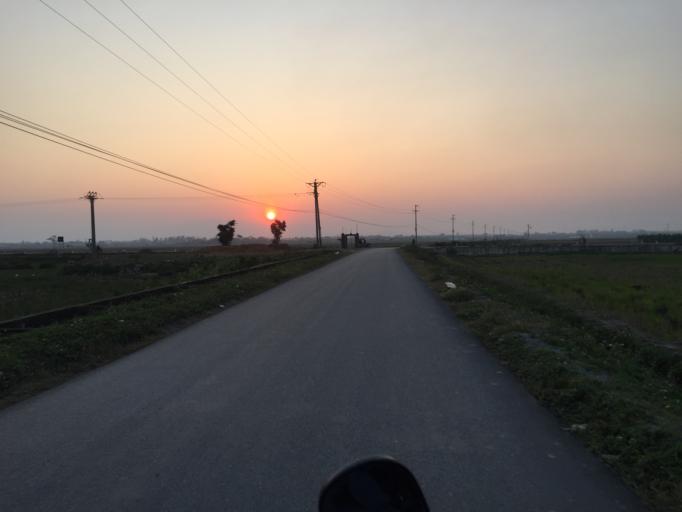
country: VN
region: Ha Noi
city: Chuc Son
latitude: 20.8916
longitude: 105.7189
